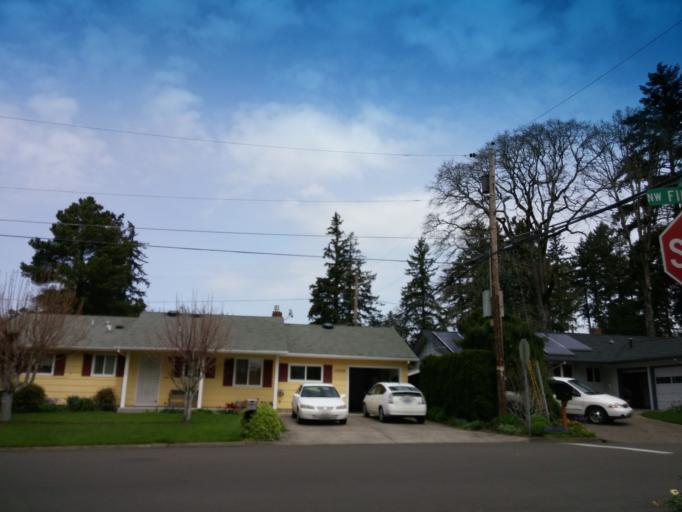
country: US
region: Oregon
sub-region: Washington County
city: Cedar Mill
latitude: 45.5279
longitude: -122.8110
